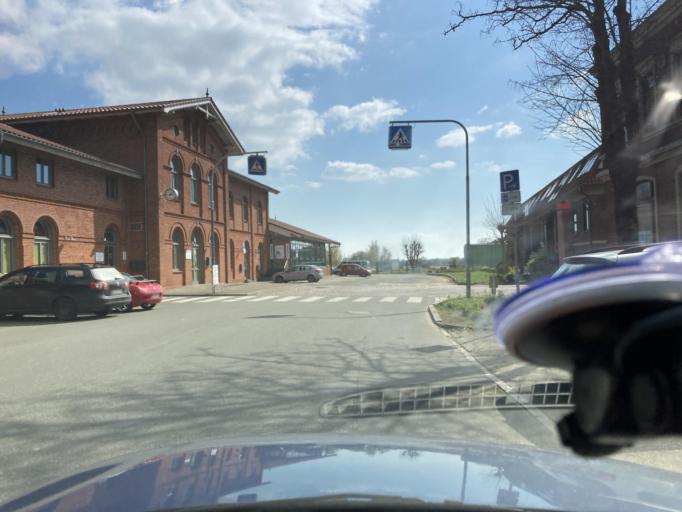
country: DE
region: Schleswig-Holstein
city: Meldorf
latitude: 54.0879
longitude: 9.0795
